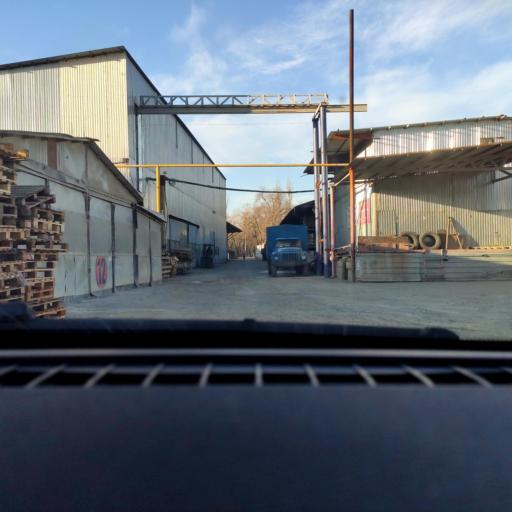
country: RU
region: Voronezj
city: Maslovka
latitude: 51.6097
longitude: 39.2482
